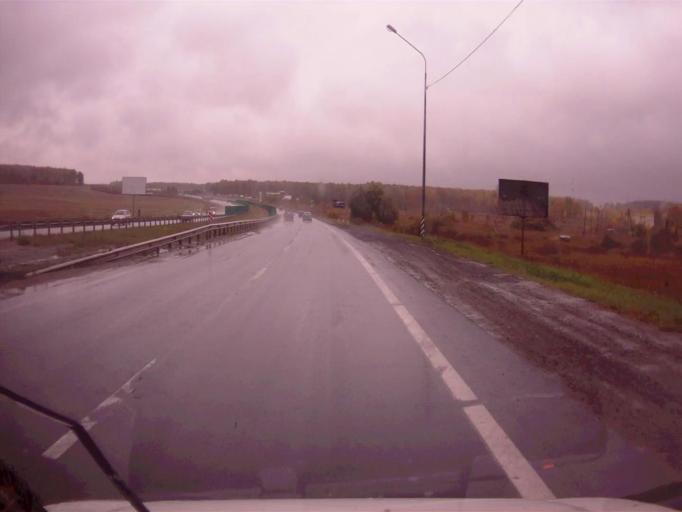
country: RU
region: Chelyabinsk
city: Dolgoderevenskoye
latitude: 55.3207
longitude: 61.3341
